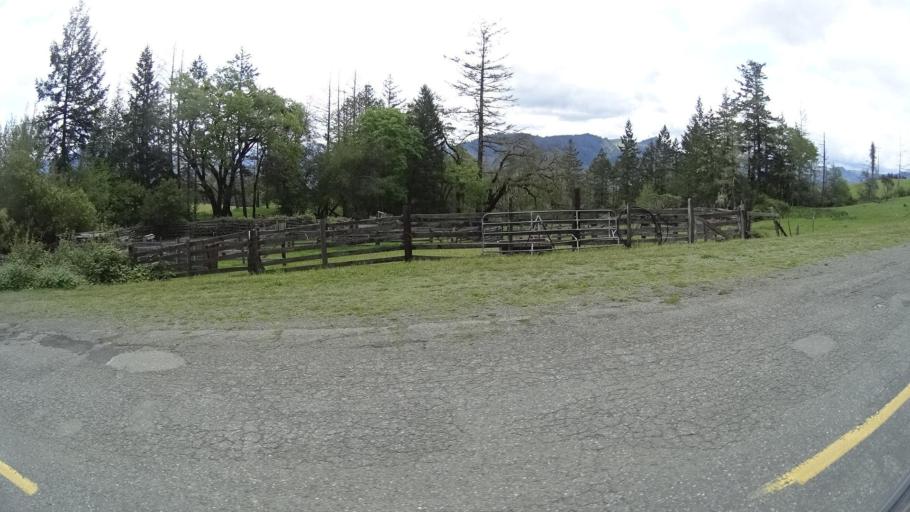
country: US
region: California
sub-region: Humboldt County
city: Redway
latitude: 40.1310
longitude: -123.6322
